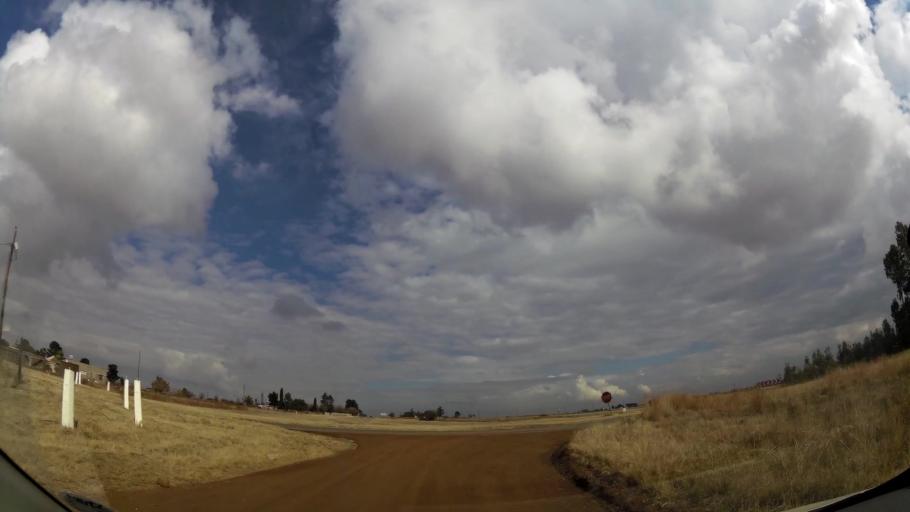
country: ZA
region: Gauteng
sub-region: Sedibeng District Municipality
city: Meyerton
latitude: -26.6065
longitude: 28.0752
